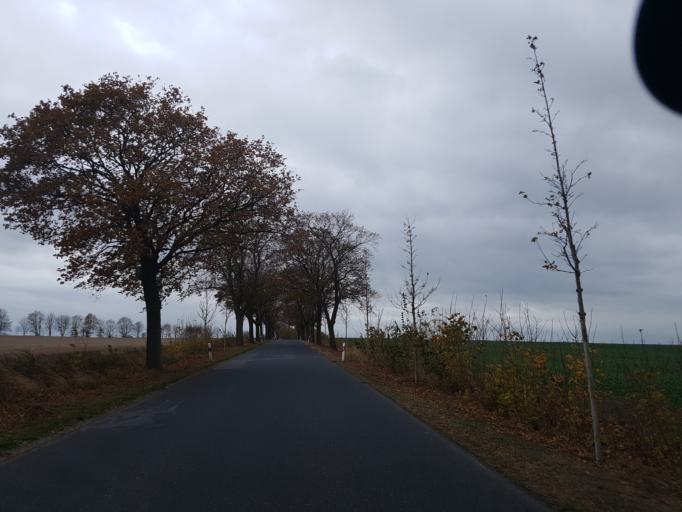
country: DE
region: Brandenburg
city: Juterbog
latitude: 51.9385
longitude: 13.0594
